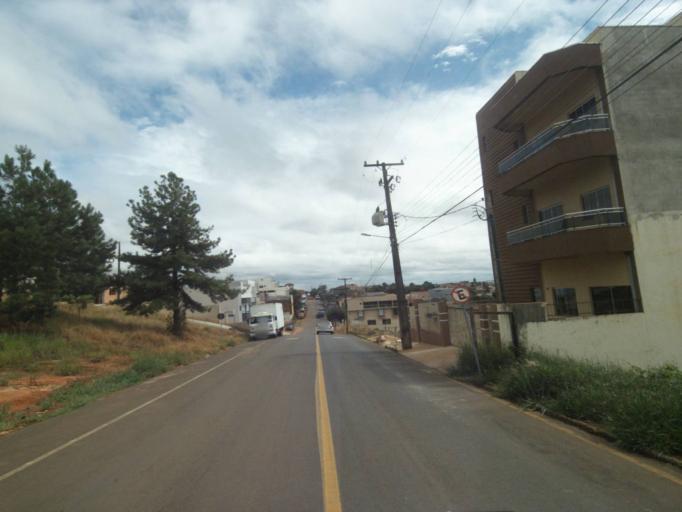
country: BR
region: Parana
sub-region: Telemaco Borba
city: Telemaco Borba
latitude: -24.3331
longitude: -50.6448
